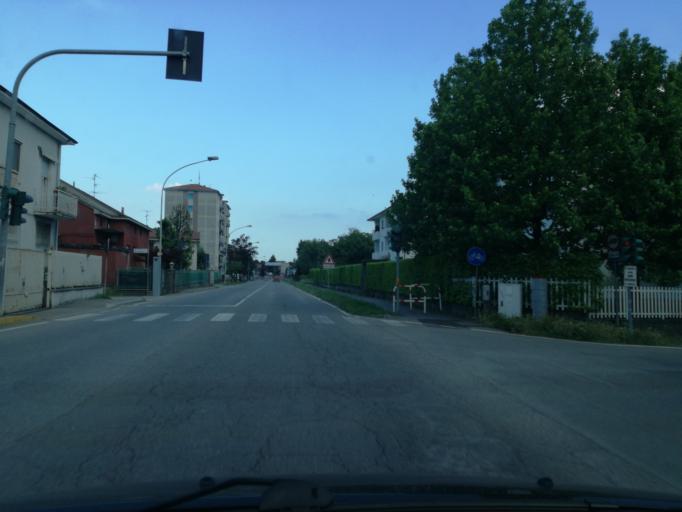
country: IT
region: Lombardy
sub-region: Provincia di Monza e Brianza
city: Porto d'Adda
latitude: 45.6499
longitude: 9.4623
